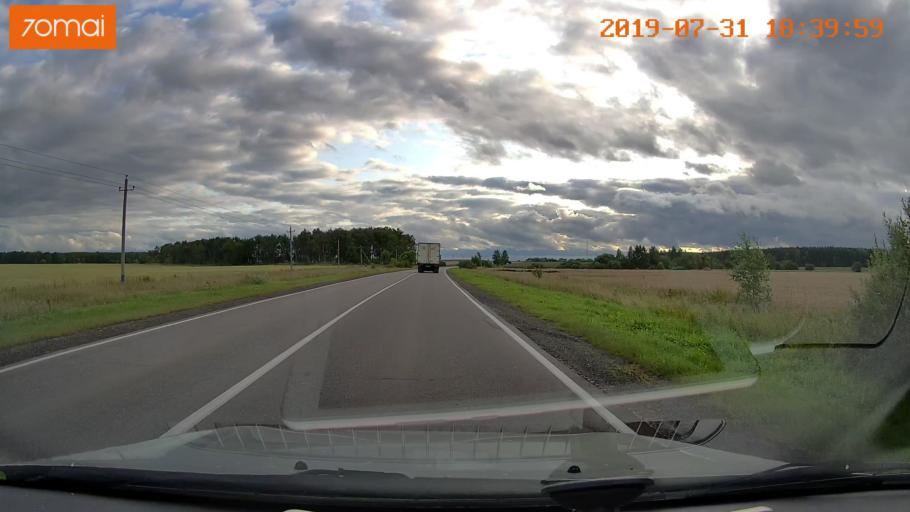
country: RU
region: Moskovskaya
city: Voskresensk
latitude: 55.2638
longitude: 38.6380
